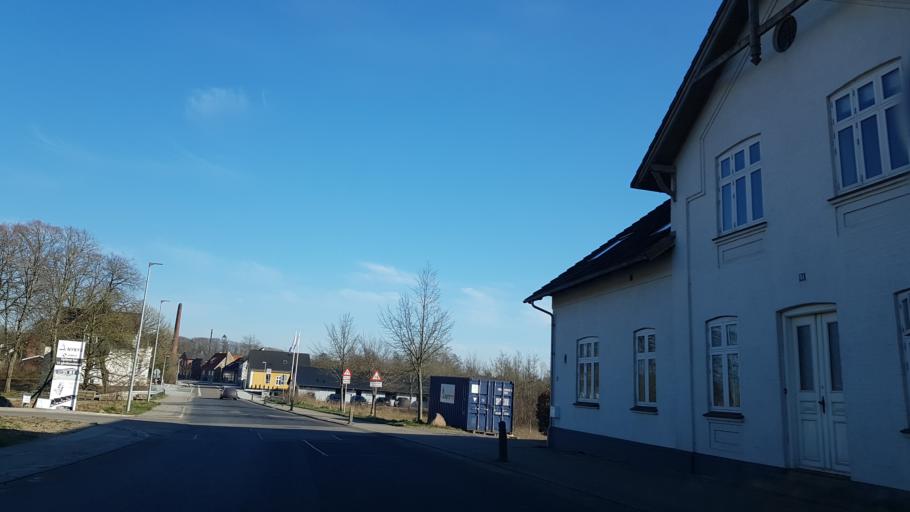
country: DK
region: South Denmark
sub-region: Kolding Kommune
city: Lunderskov
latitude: 55.4801
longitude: 9.2948
